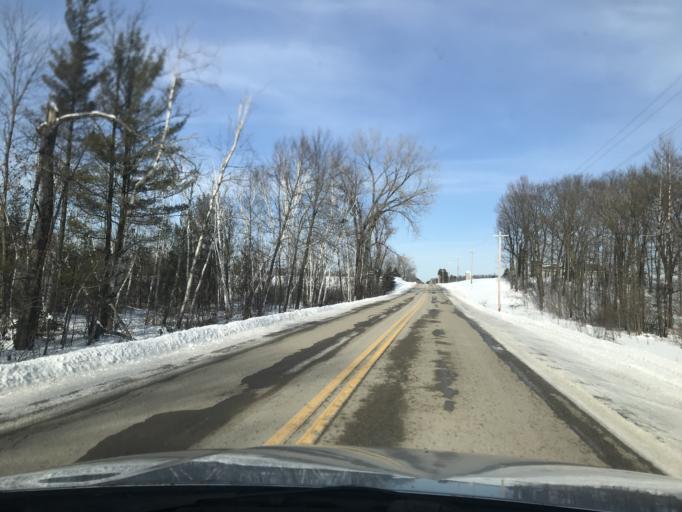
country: US
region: Wisconsin
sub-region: Oconto County
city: Oconto Falls
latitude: 45.1497
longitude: -88.1877
